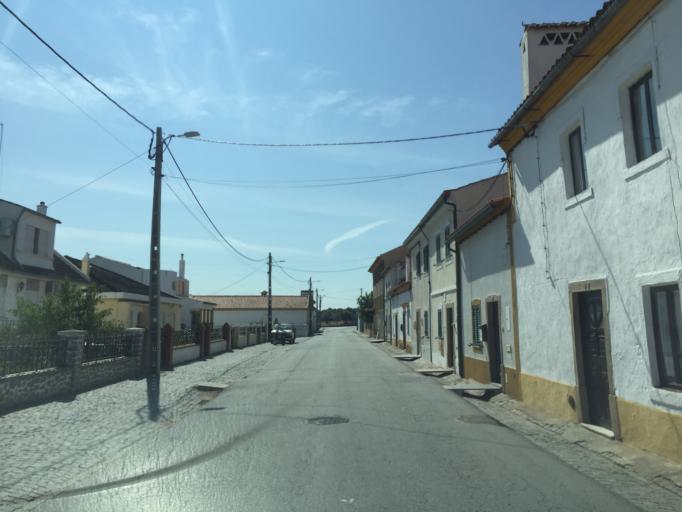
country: PT
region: Portalegre
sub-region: Portalegre
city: Alagoa
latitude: 39.4167
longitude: -7.6164
